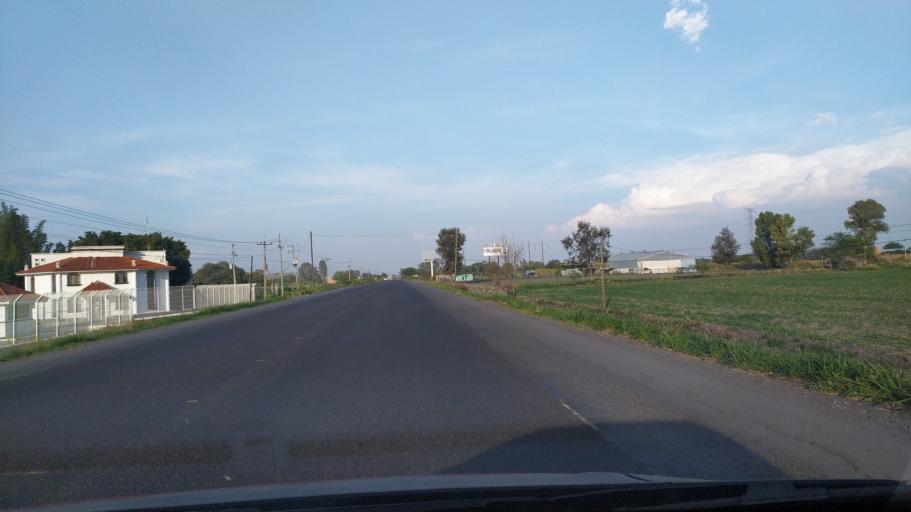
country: MX
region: Jalisco
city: Jamay
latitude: 20.2943
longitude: -102.6605
